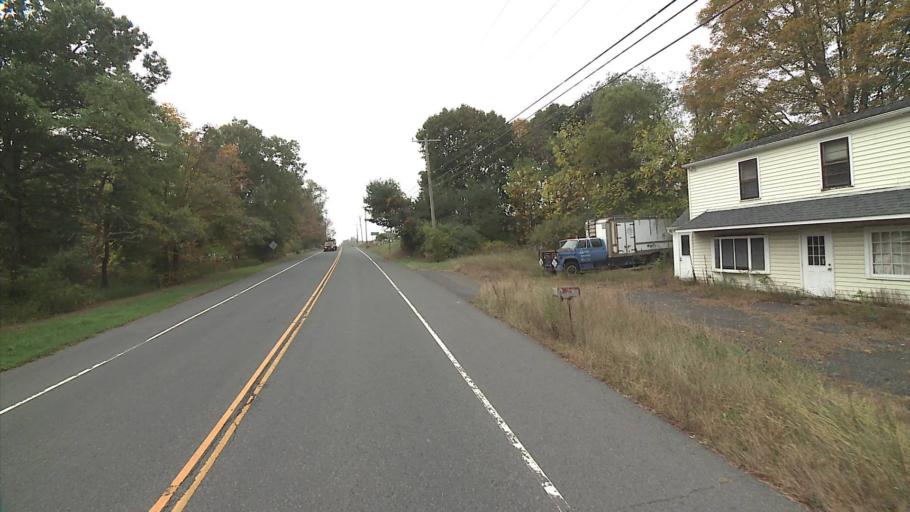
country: US
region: Connecticut
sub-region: Litchfield County
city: Watertown
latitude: 41.5932
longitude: -73.1705
